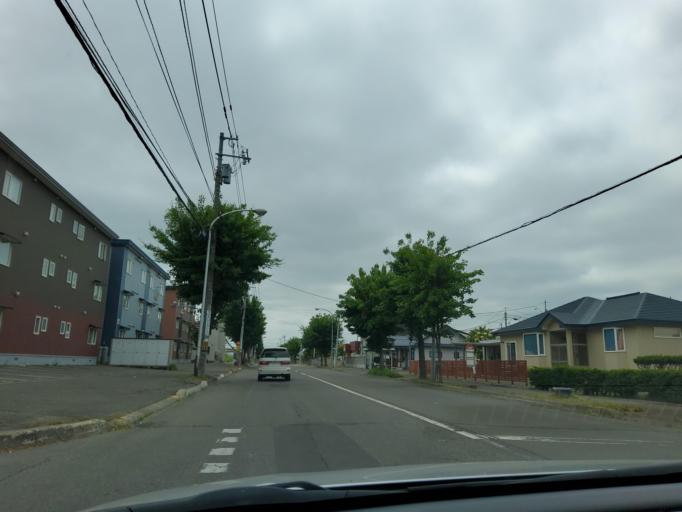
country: JP
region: Hokkaido
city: Obihiro
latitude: 42.9145
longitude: 143.1695
